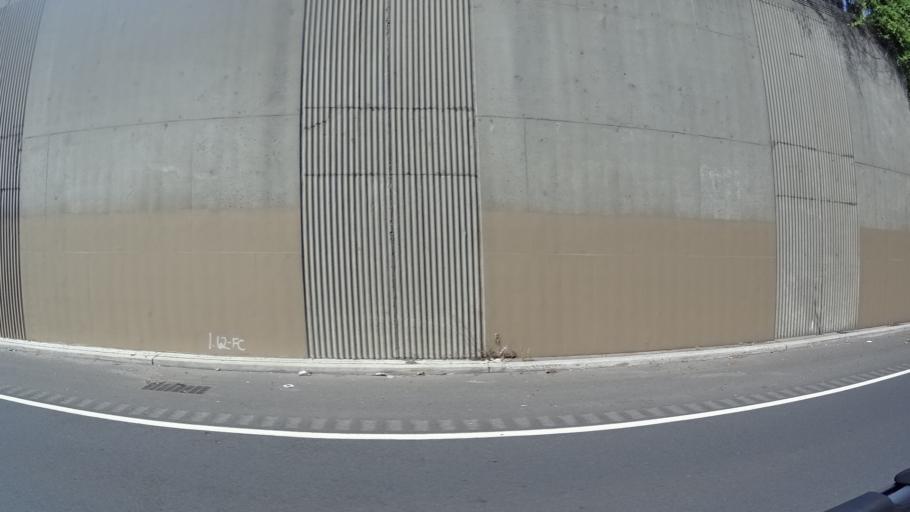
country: US
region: New Jersey
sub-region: Union County
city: Hillside
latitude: 40.7080
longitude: -74.2324
